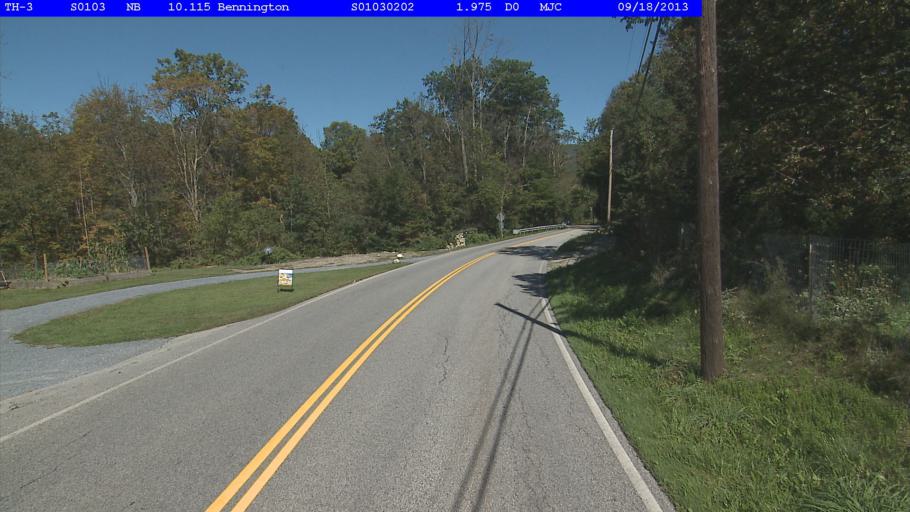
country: US
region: Vermont
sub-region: Bennington County
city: Bennington
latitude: 42.8646
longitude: -73.1759
